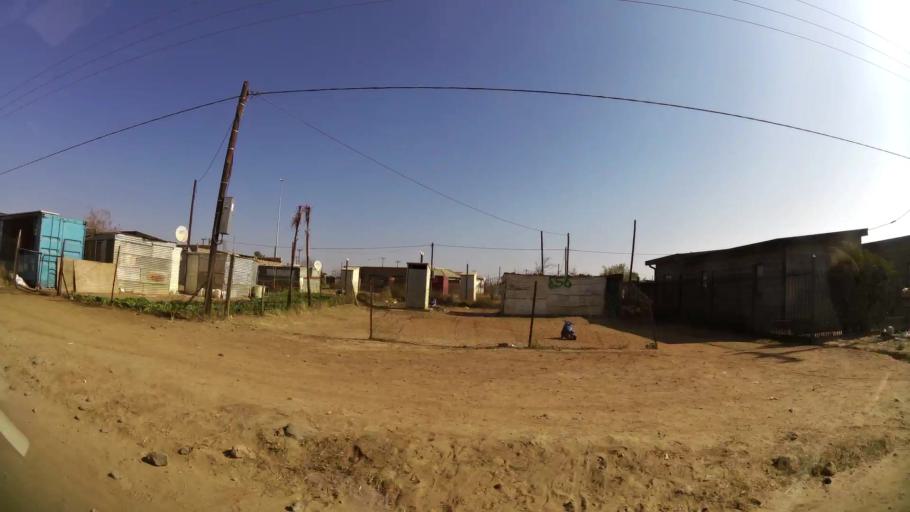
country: ZA
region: Orange Free State
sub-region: Mangaung Metropolitan Municipality
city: Bloemfontein
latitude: -29.1785
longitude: 26.2882
